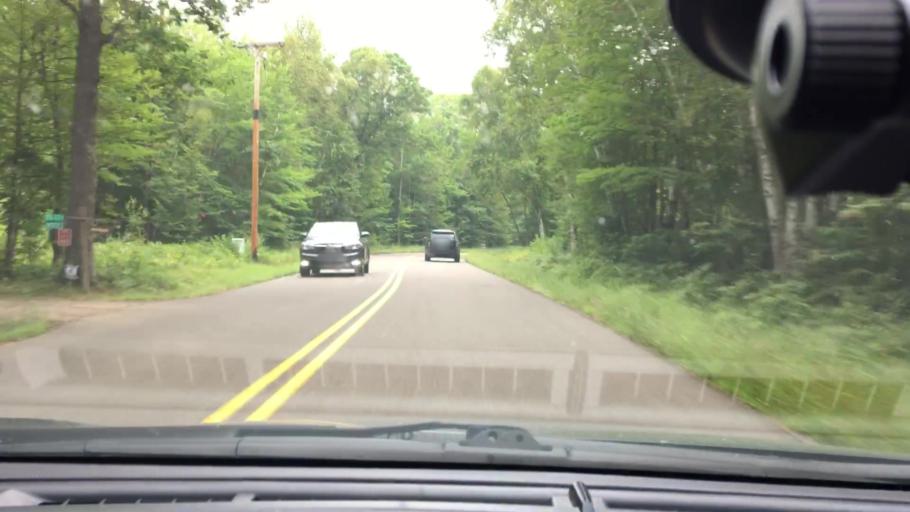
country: US
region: Minnesota
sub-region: Crow Wing County
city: Cross Lake
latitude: 46.6708
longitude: -94.0398
